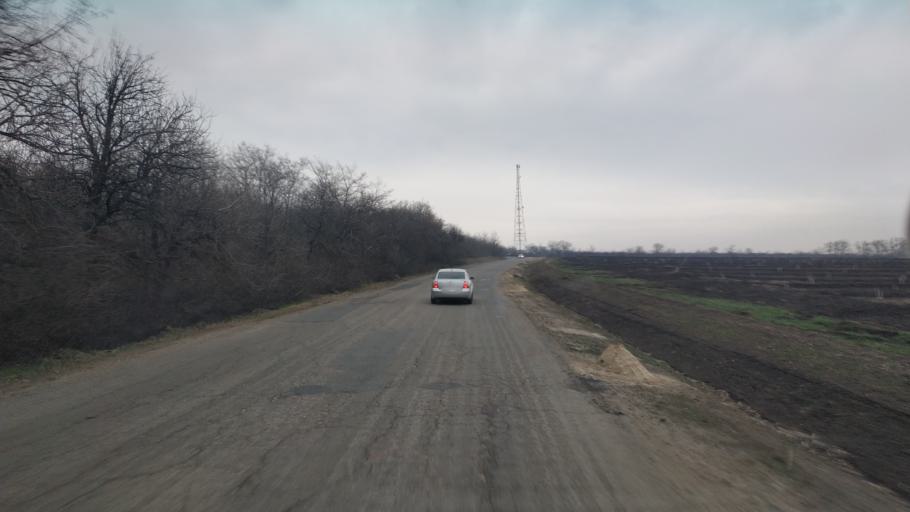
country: MD
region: Chisinau
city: Singera
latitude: 46.8576
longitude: 29.0266
